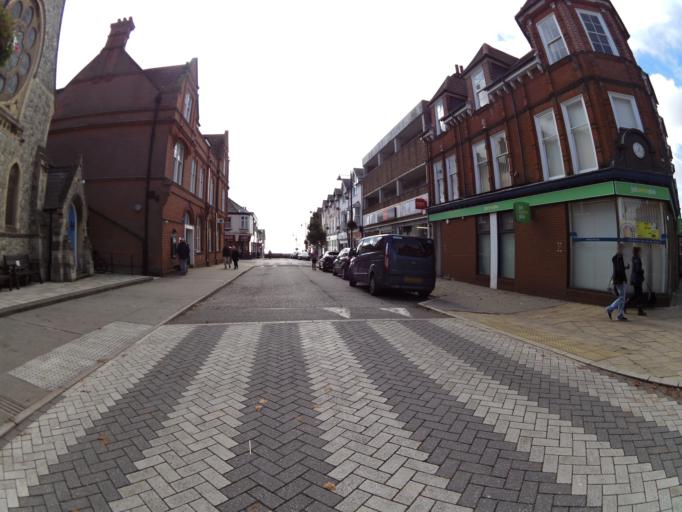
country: GB
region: England
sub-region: Suffolk
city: Felixstowe
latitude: 51.9616
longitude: 1.3513
